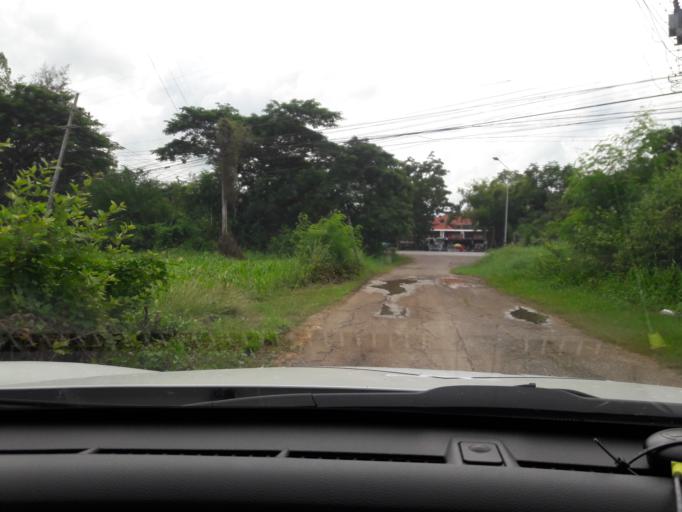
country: TH
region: Nakhon Sawan
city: Tak Fa
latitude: 15.3570
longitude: 100.5030
